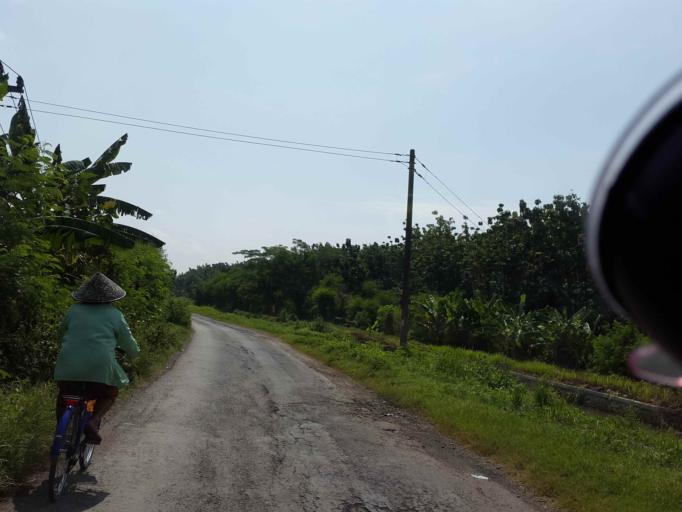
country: ID
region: Central Java
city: Pemalang
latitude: -6.9517
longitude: 109.3612
